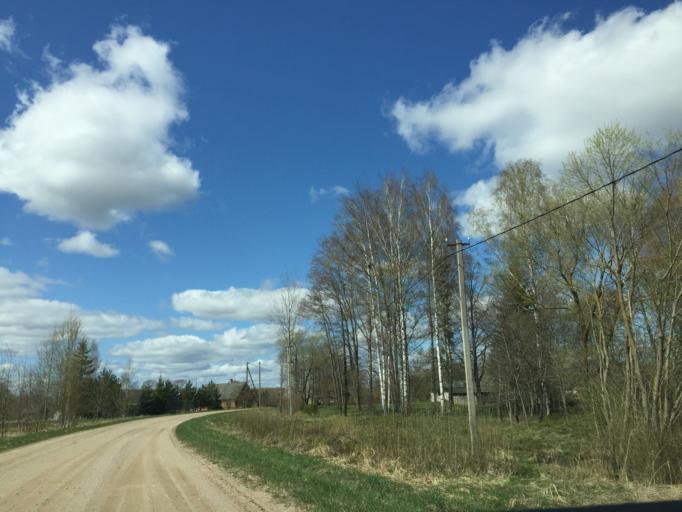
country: LV
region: Vilanu
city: Vilani
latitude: 56.6523
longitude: 27.1297
